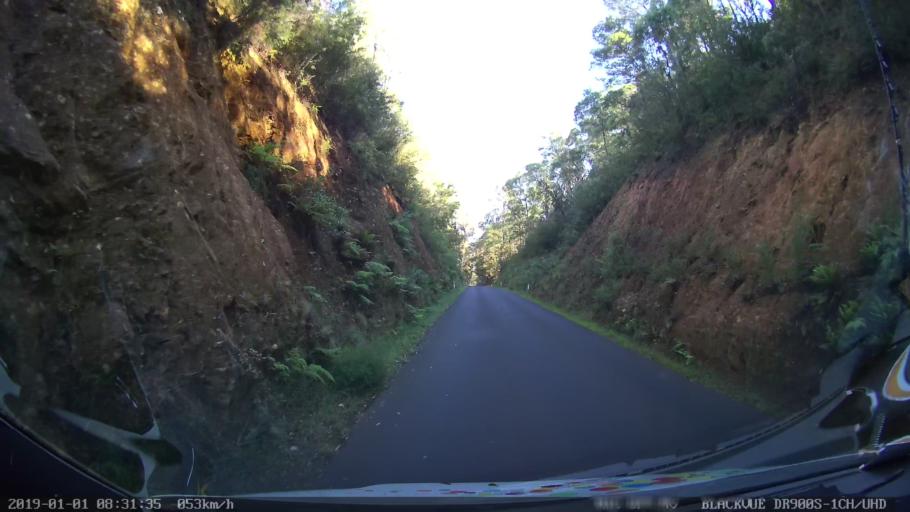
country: AU
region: New South Wales
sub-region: Snowy River
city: Jindabyne
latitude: -36.3690
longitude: 148.2052
